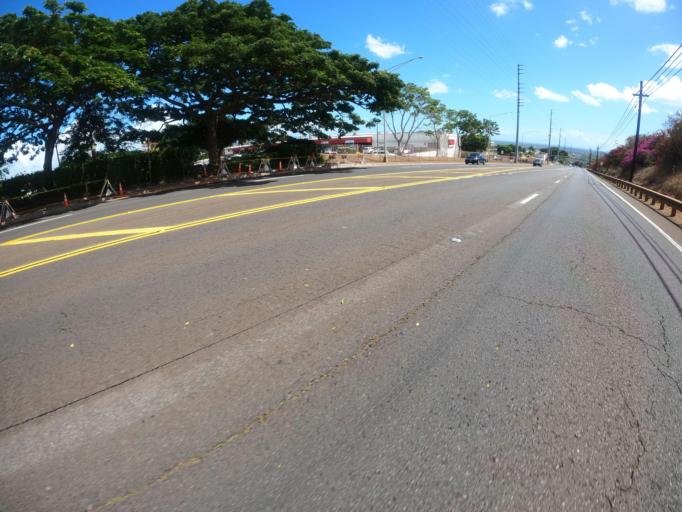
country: US
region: Hawaii
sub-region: Honolulu County
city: Royal Kunia
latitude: 21.3900
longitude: -158.0352
